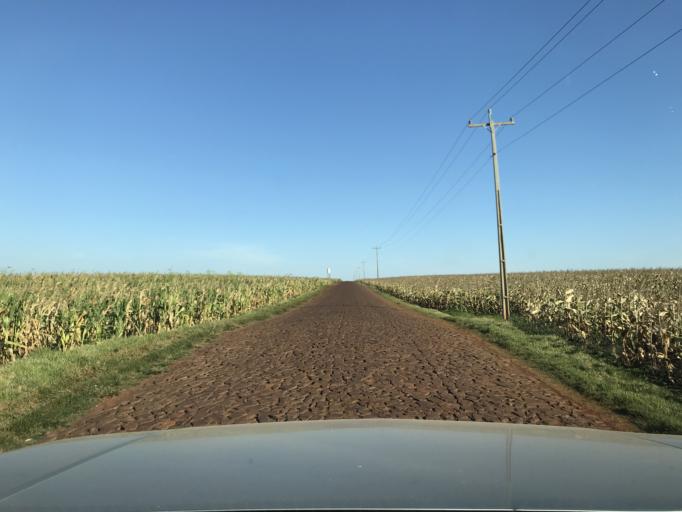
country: BR
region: Parana
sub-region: Palotina
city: Palotina
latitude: -24.2335
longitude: -53.8235
